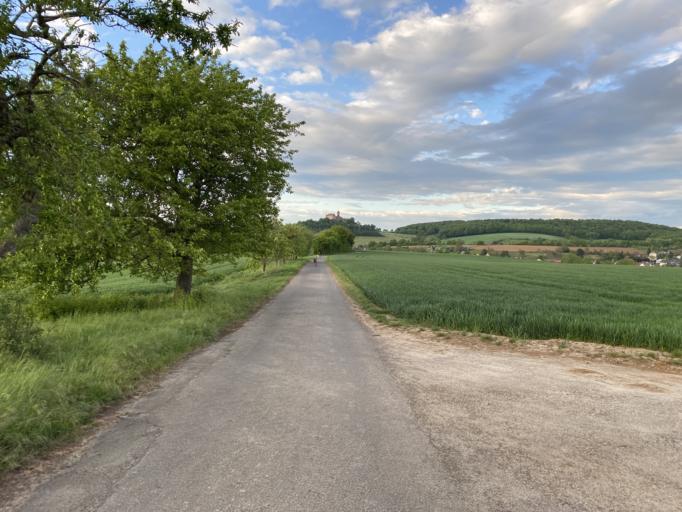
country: DE
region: Hesse
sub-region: Regierungsbezirk Darmstadt
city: Langenselbold
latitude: 50.2257
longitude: 9.0494
